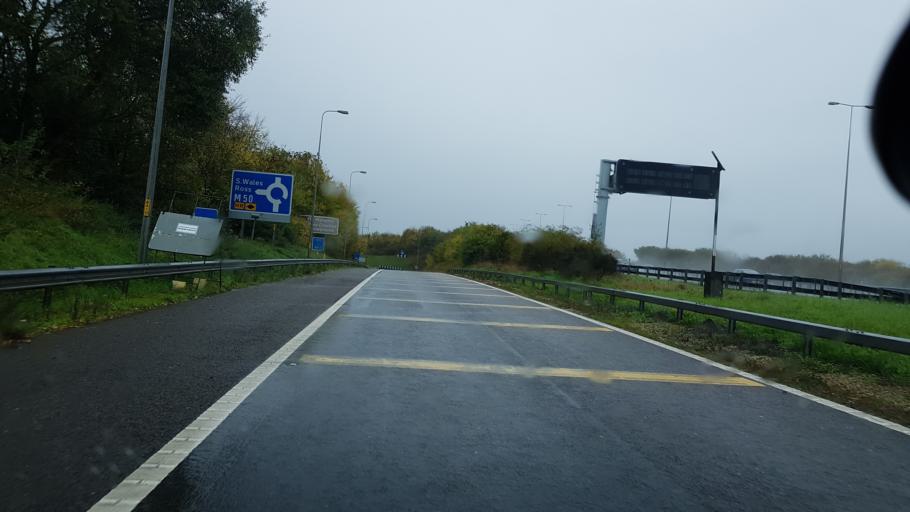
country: GB
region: England
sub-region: Worcestershire
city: Bredon
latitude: 52.0450
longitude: -2.1344
